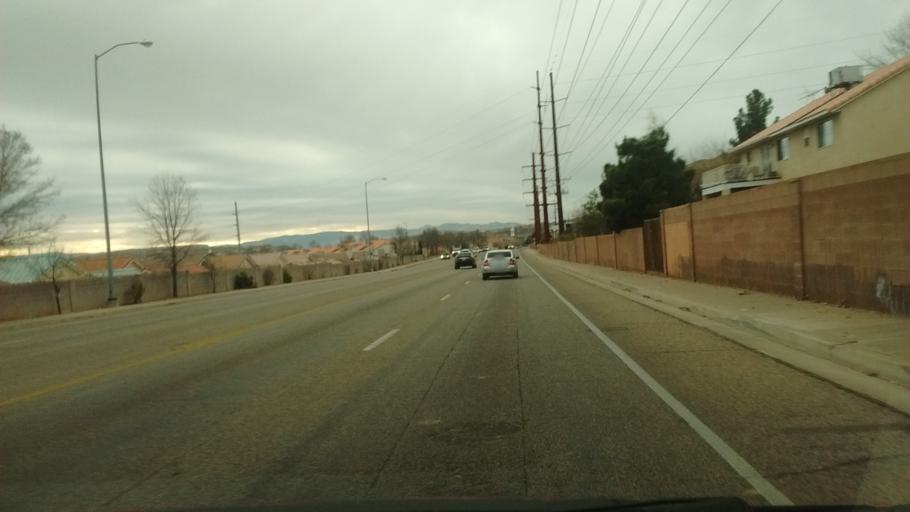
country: US
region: Utah
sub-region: Washington County
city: Washington
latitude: 37.1074
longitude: -113.5260
